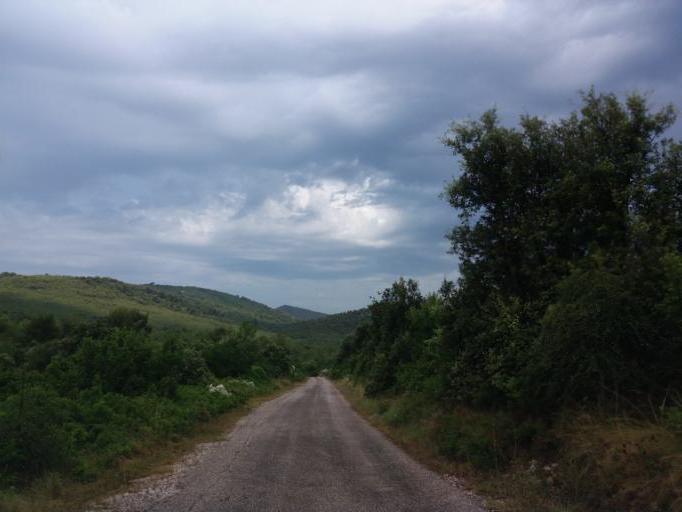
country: HR
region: Zadarska
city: Sali
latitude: 43.9123
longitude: 15.1352
